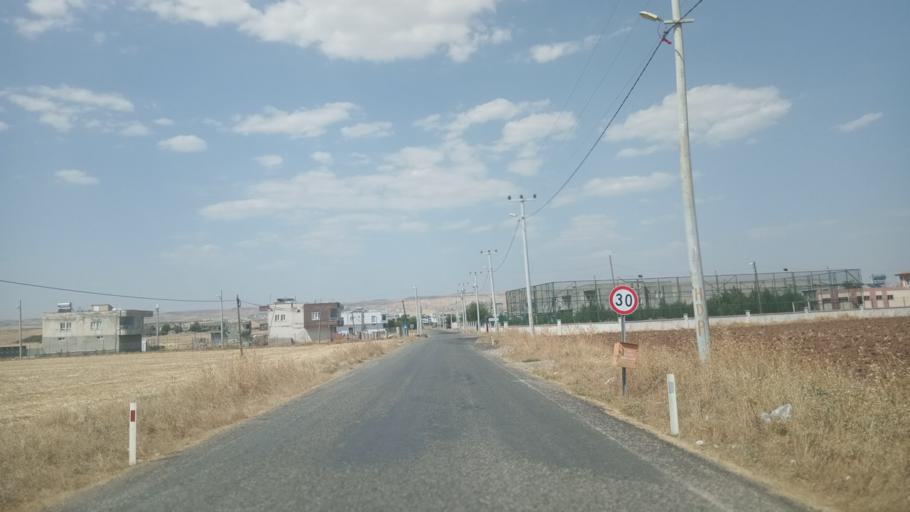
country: TR
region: Batman
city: Binatli
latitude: 37.8391
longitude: 41.2092
